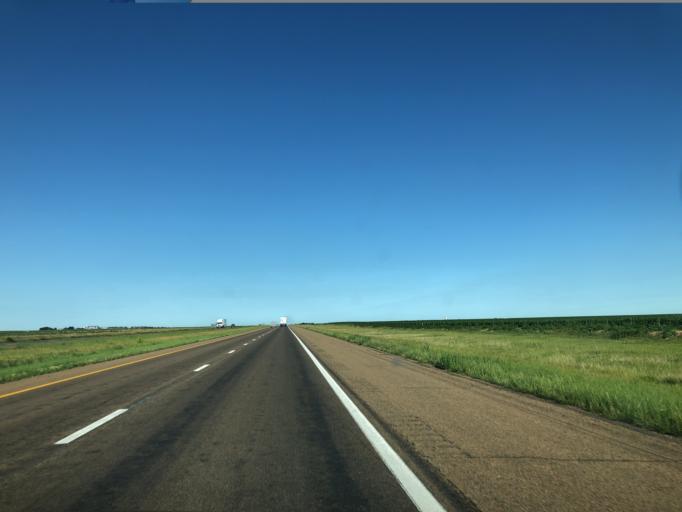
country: US
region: Kansas
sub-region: Thomas County
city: Colby
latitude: 39.3651
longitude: -101.1037
